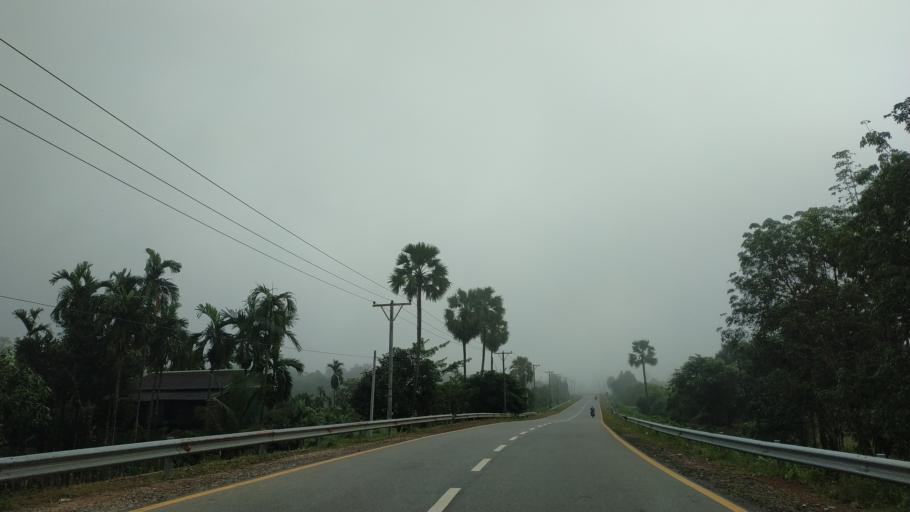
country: MM
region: Tanintharyi
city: Dawei
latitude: 14.1604
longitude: 98.2050
